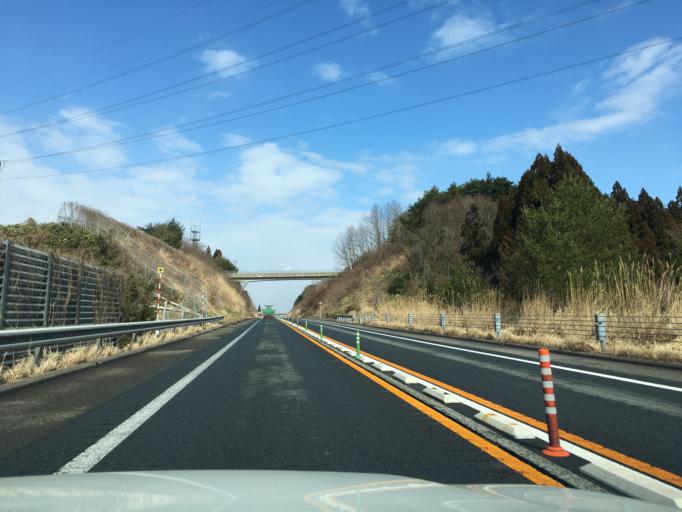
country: JP
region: Akita
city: Akita Shi
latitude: 39.8073
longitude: 140.0947
